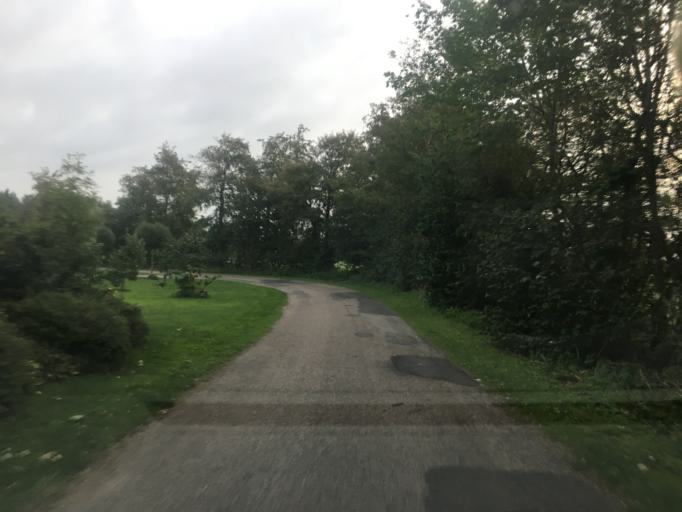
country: DK
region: South Denmark
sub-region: Tonder Kommune
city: Logumkloster
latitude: 54.9838
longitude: 9.0100
